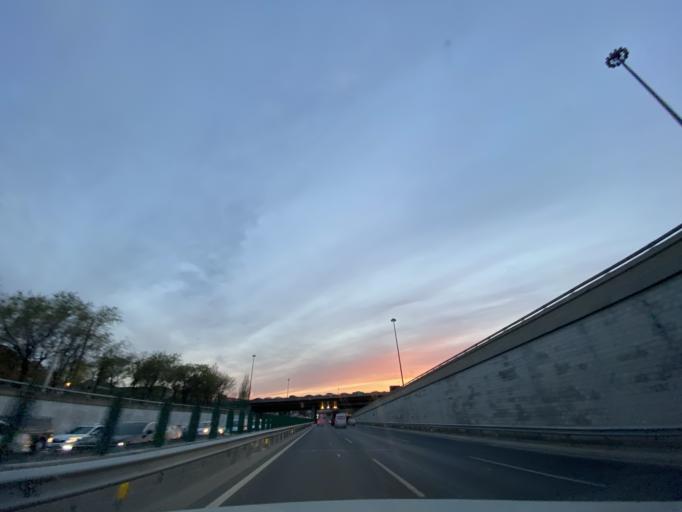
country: CN
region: Beijing
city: Haidian
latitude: 40.0124
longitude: 116.2831
